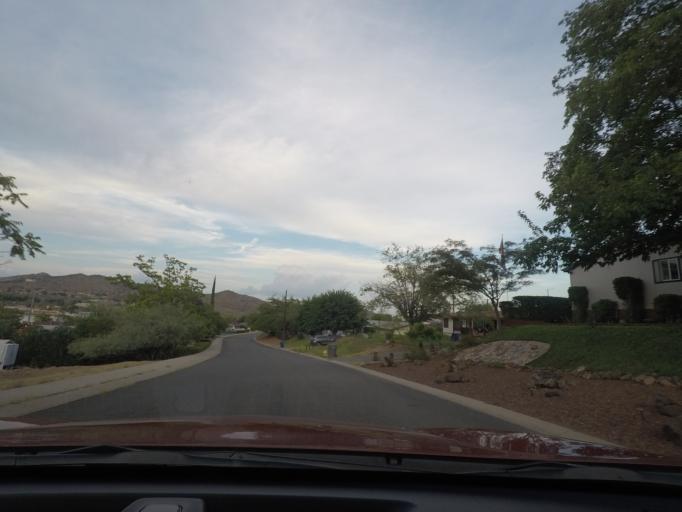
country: US
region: Arizona
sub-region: Yavapai County
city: Bagdad
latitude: 34.5717
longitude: -113.1822
